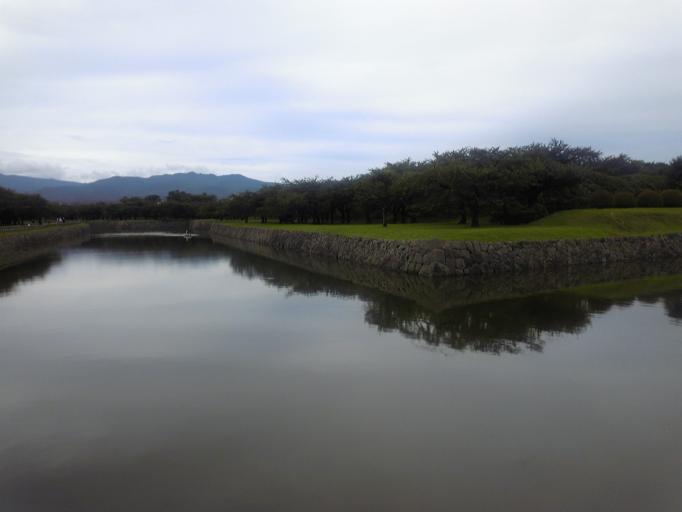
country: JP
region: Hokkaido
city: Hakodate
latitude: 41.7958
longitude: 140.7541
